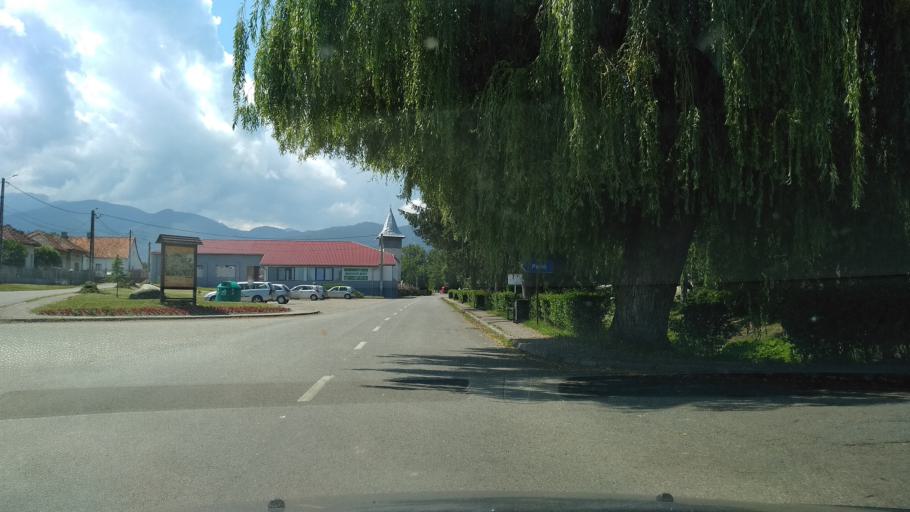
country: RO
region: Hunedoara
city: Salasu de Sus
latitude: 45.5102
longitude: 22.9548
